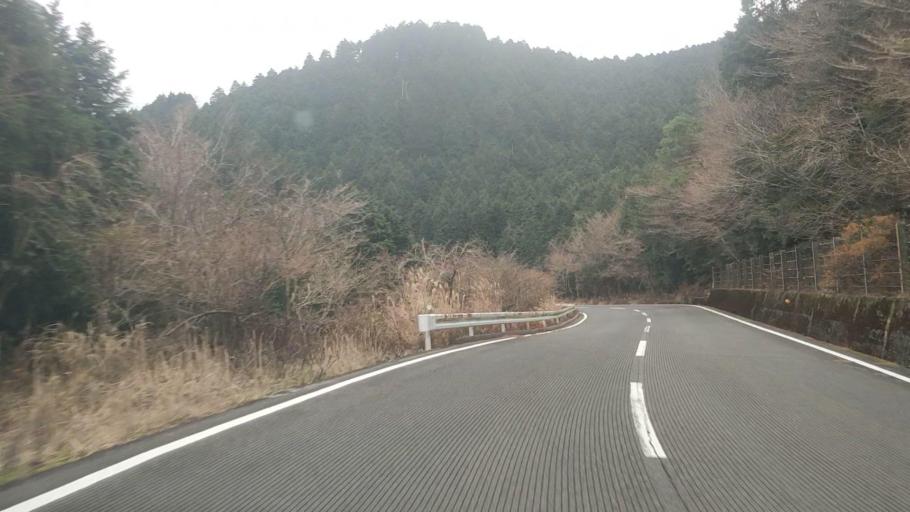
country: JP
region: Nagasaki
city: Shimabara
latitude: 32.7673
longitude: 130.2720
